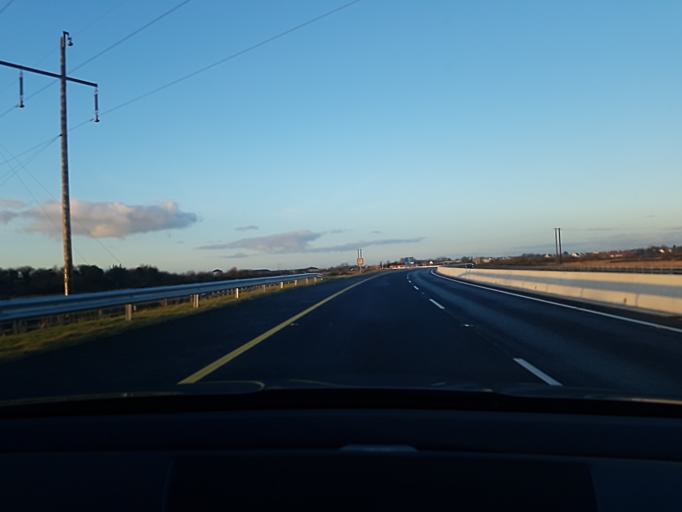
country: IE
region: Connaught
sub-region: County Galway
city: Tuam
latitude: 53.5000
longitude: -8.8787
